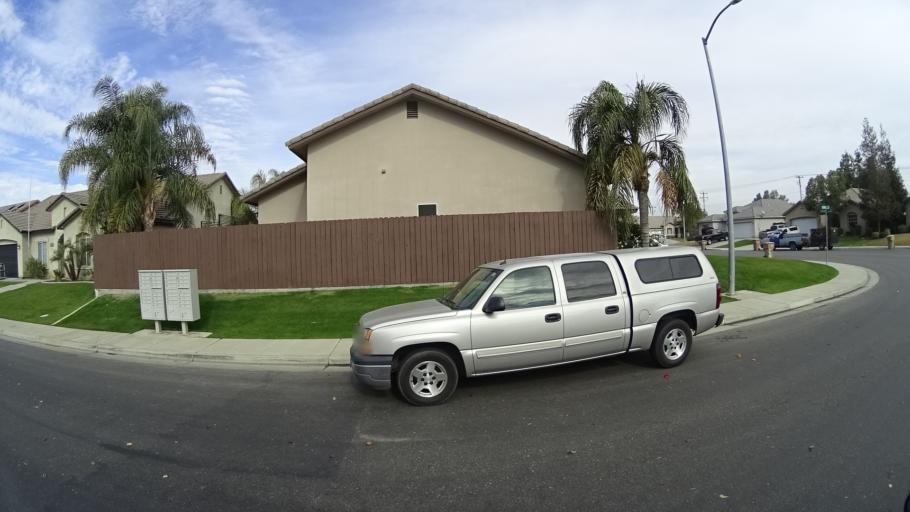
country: US
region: California
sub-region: Kern County
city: Rosedale
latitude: 35.3941
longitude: -119.1289
